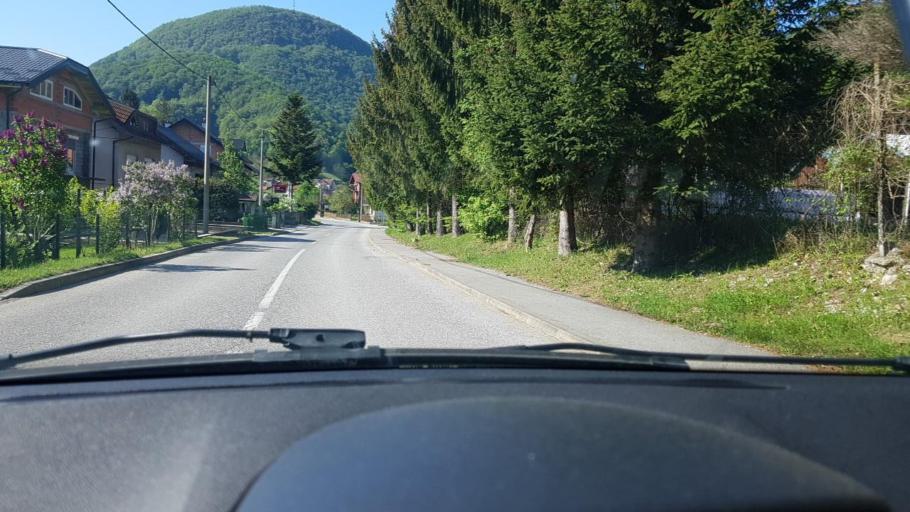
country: HR
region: Krapinsko-Zagorska
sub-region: Grad Krapina
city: Krapina
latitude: 46.1995
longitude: 15.8415
